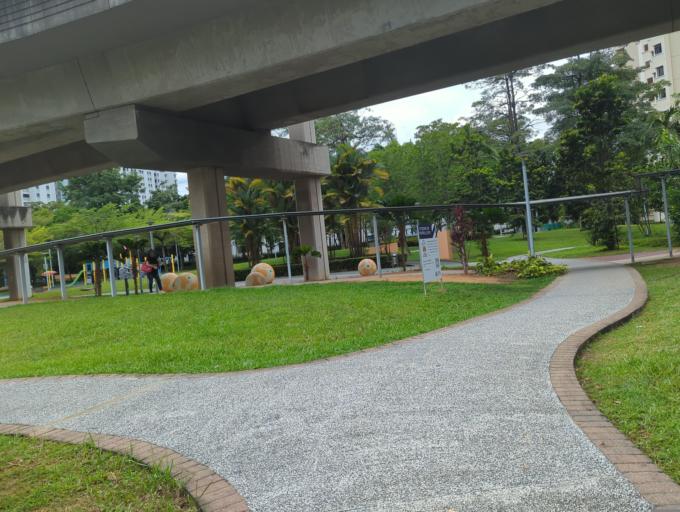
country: MY
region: Johor
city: Kampung Pasir Gudang Baru
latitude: 1.3944
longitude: 103.8964
